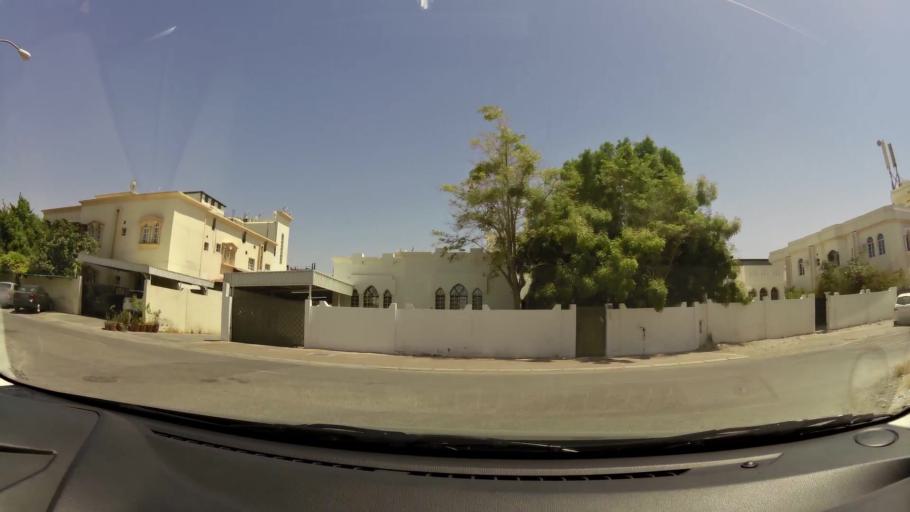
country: OM
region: Muhafazat Masqat
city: Bawshar
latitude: 23.5933
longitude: 58.3763
